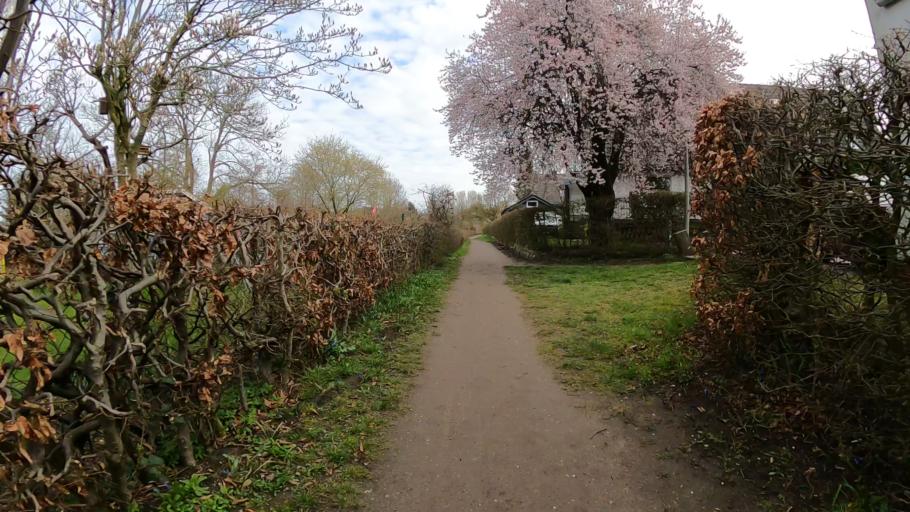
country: DE
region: Hamburg
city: Steilshoop
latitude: 53.5939
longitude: 10.0704
